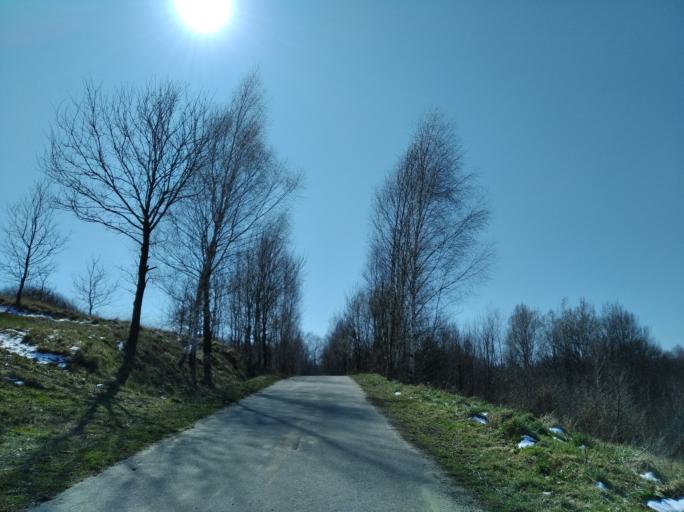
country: PL
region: Subcarpathian Voivodeship
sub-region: Powiat strzyzowski
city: Strzyzow
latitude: 49.8591
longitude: 21.8119
